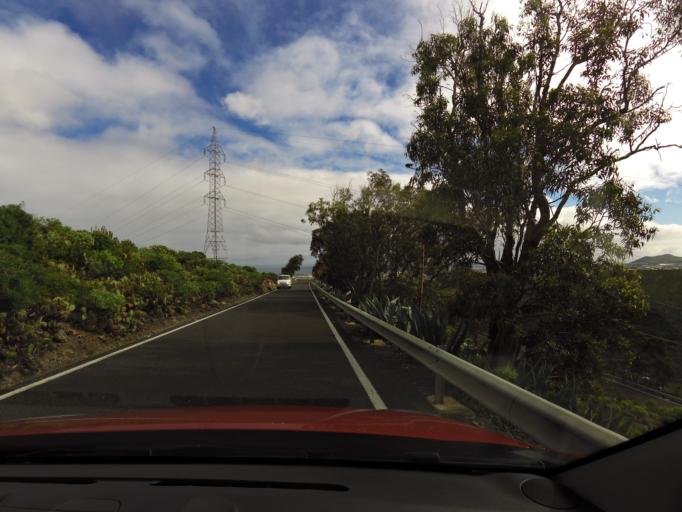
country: ES
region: Canary Islands
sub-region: Provincia de Las Palmas
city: Telde
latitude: 28.0125
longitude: -15.4369
